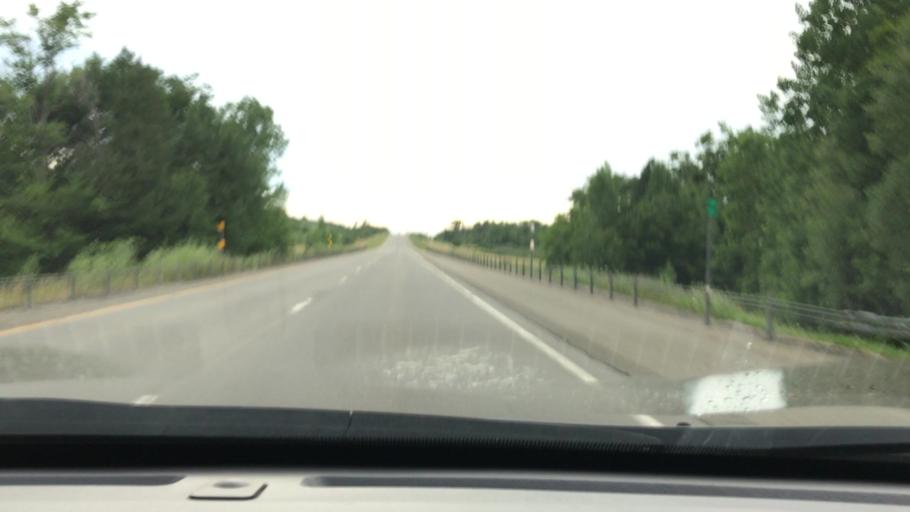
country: US
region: New York
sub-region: Erie County
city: North Boston
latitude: 42.5990
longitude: -78.7466
